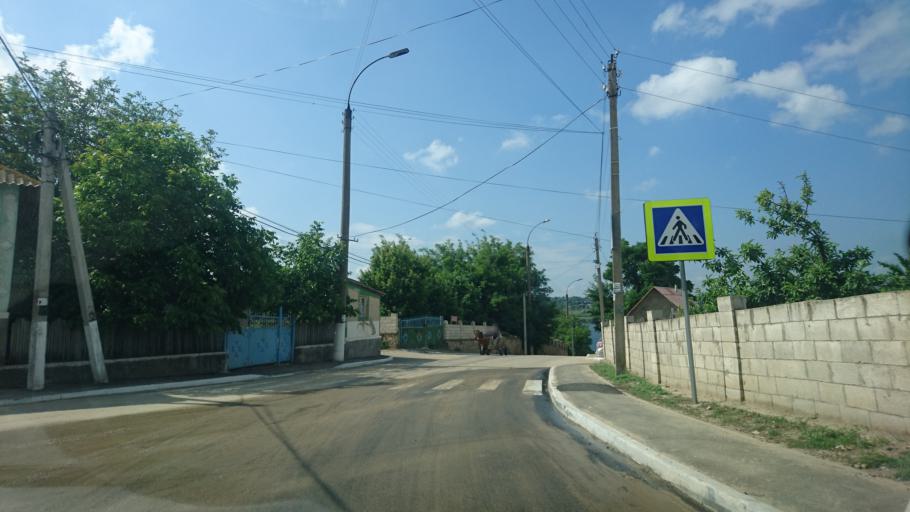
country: MD
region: Telenesti
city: Cocieri
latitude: 47.3556
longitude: 29.1065
